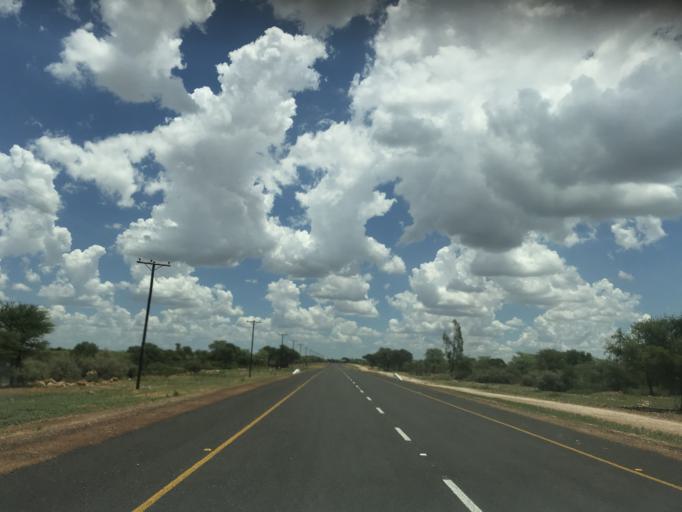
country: BW
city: Mabuli
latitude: -25.8038
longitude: 24.8260
